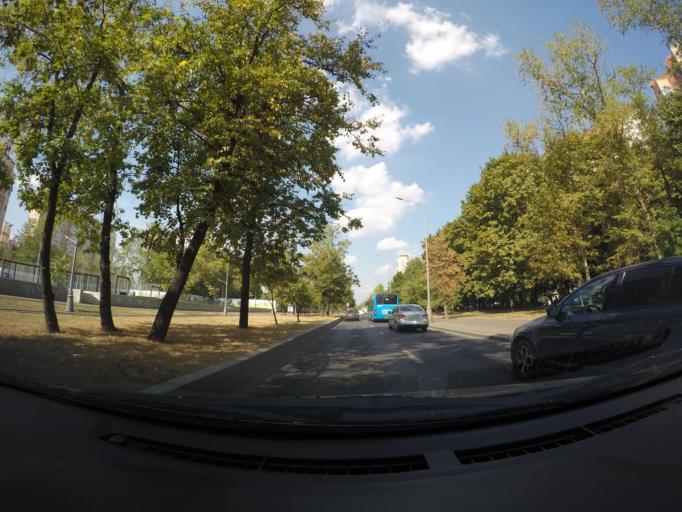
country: RU
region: Moskovskaya
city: Levoberezhnaya
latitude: 55.8700
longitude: 37.4838
